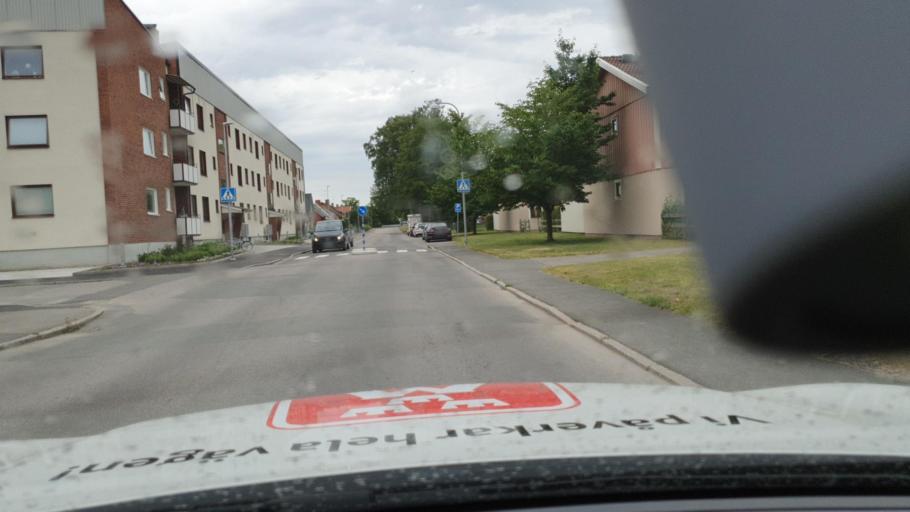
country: SE
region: Vaestra Goetaland
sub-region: Hjo Kommun
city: Hjo
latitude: 58.3081
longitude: 14.2939
